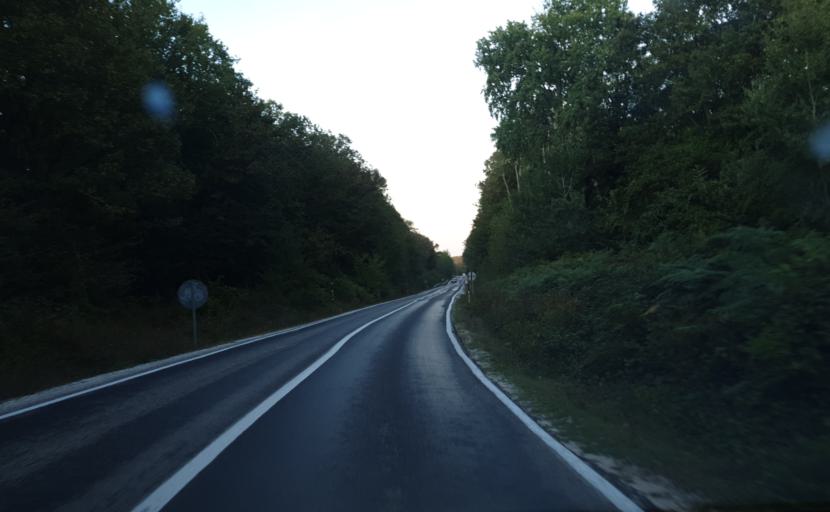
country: TR
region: Kirklareli
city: Igneada
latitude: 41.8710
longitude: 27.8084
